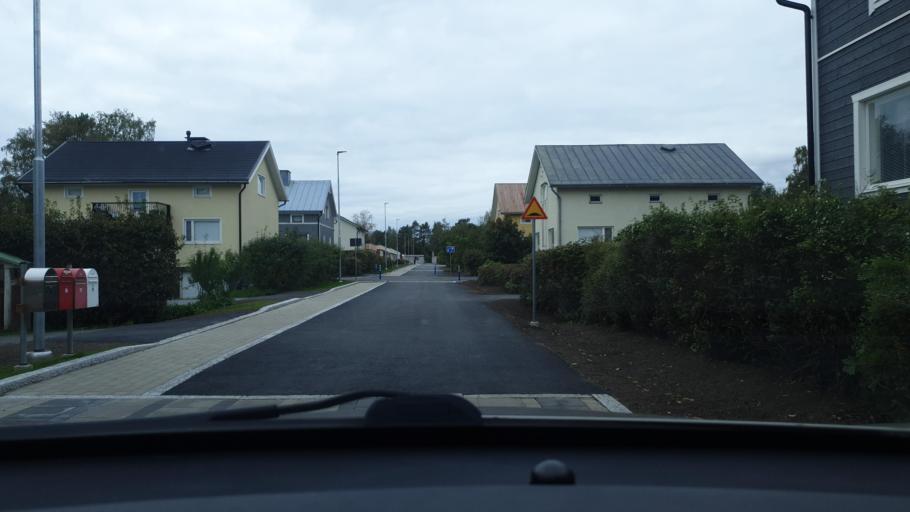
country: FI
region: Ostrobothnia
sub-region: Vaasa
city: Korsholm
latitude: 63.0952
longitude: 21.6735
